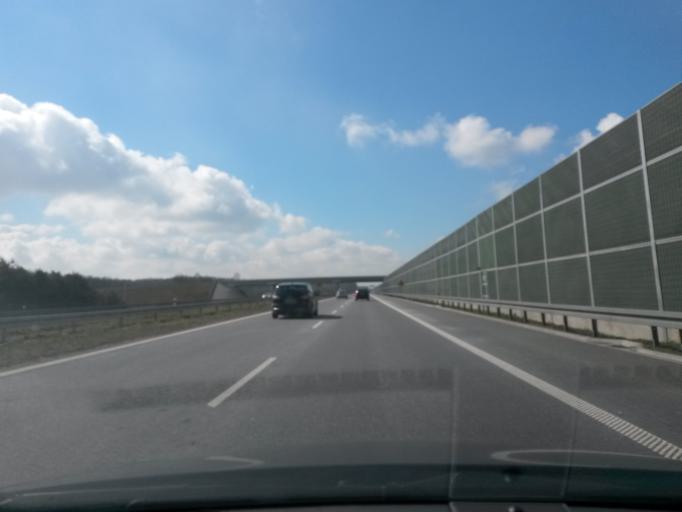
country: PL
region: Lodz Voivodeship
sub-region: powiat Lowicki
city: Nieborow
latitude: 52.0515
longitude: 20.1059
